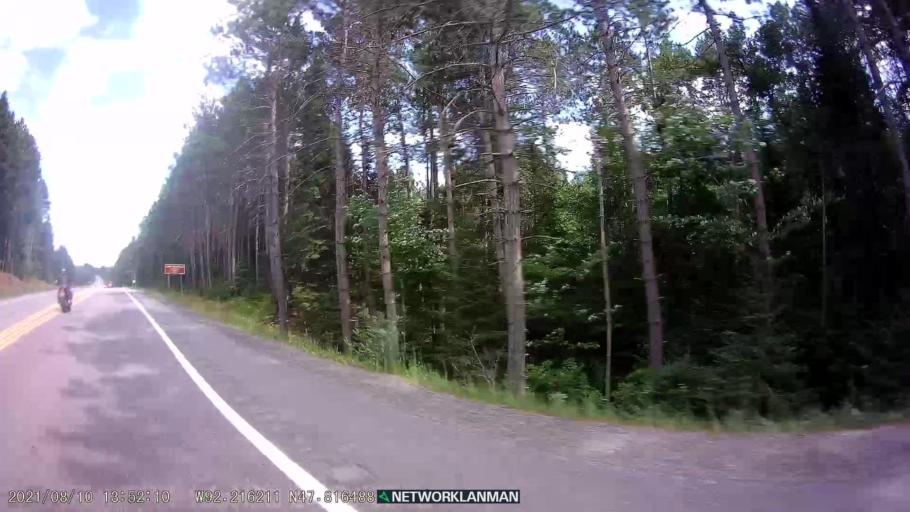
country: US
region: Minnesota
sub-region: Saint Louis County
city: Aurora
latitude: 47.8165
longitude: -92.2159
